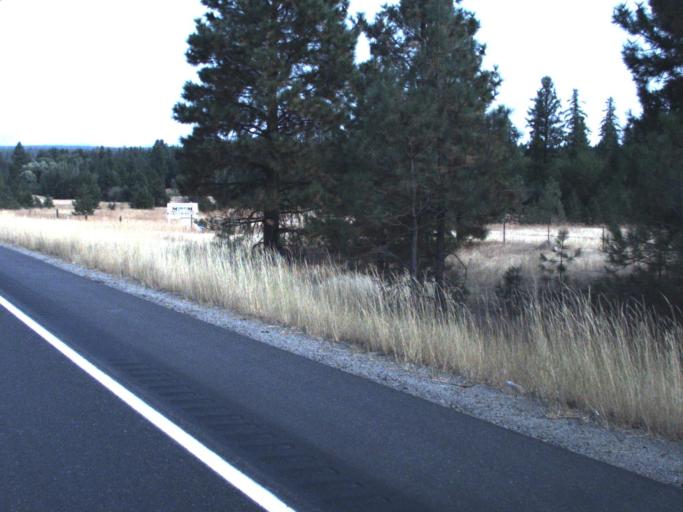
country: US
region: Washington
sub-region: Spokane County
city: Deer Park
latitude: 47.8790
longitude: -117.4222
